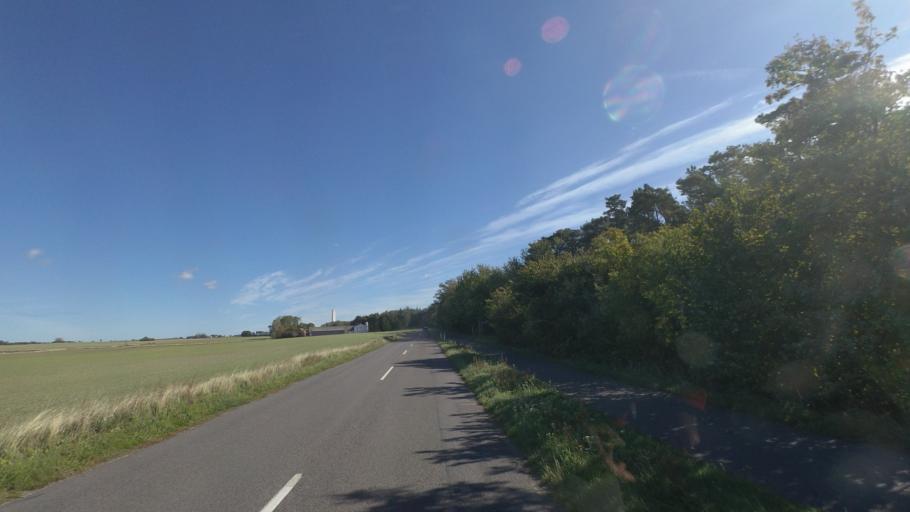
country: DK
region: Capital Region
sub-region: Bornholm Kommune
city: Nexo
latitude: 55.0018
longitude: 15.0534
